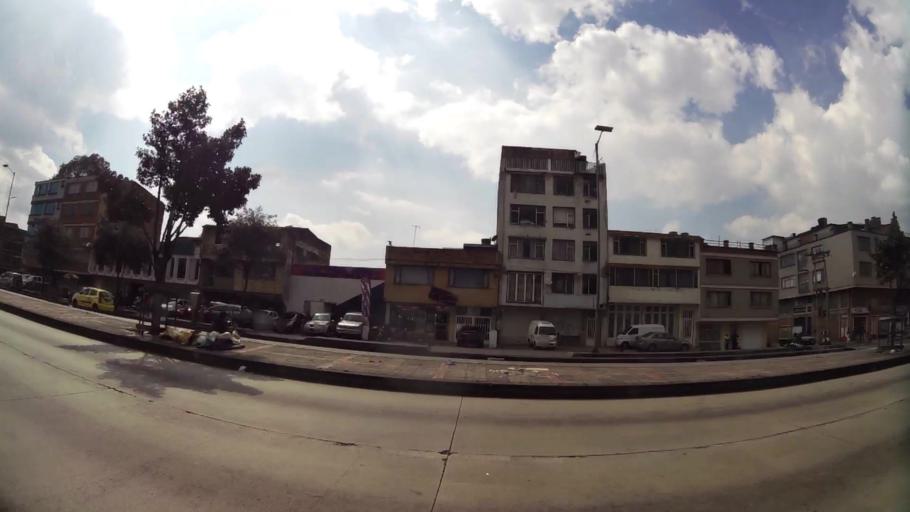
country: CO
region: Bogota D.C.
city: Bogota
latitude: 4.5893
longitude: -74.0914
